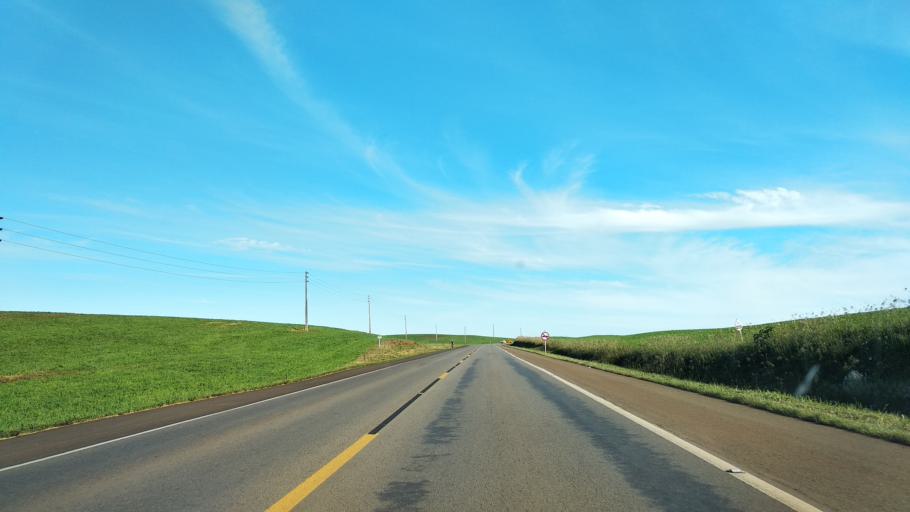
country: BR
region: Santa Catarina
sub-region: Celso Ramos
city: Celso Ramos
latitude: -27.5190
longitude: -51.3511
